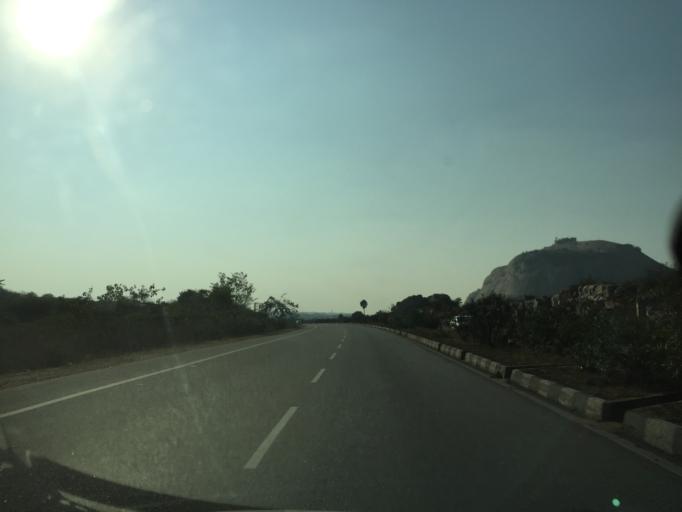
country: IN
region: Telangana
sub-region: Nalgonda
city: Bhongir
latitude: 17.5134
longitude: 78.9049
